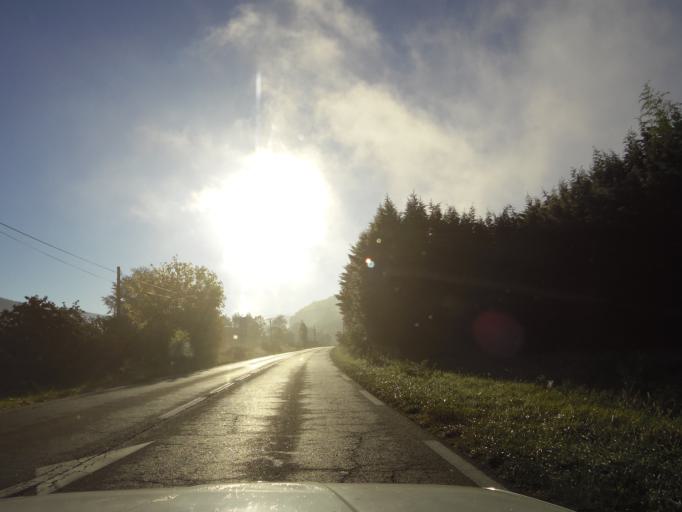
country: FR
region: Rhone-Alpes
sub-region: Departement de l'Ain
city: Saint-Sorlin-en-Bugey
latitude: 45.8746
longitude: 5.3599
